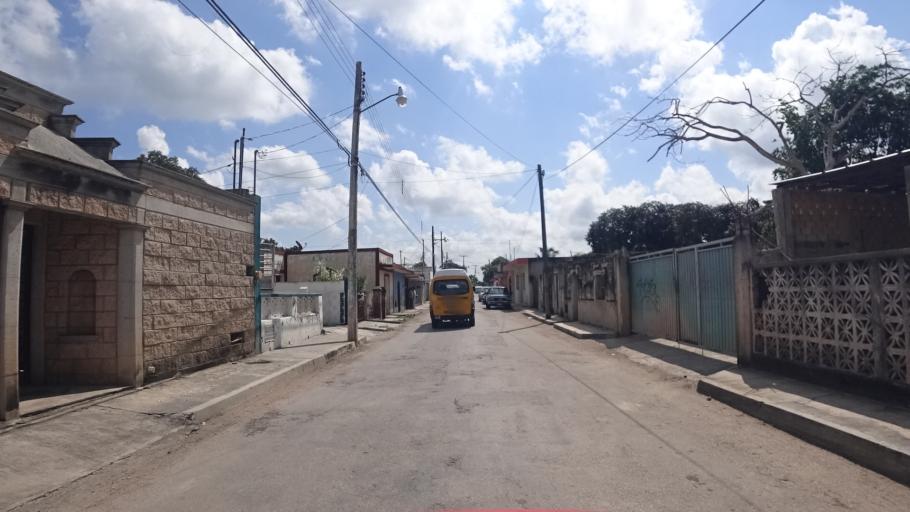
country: MX
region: Yucatan
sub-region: Tizimin
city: Tizimin
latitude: 21.1481
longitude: -88.1517
